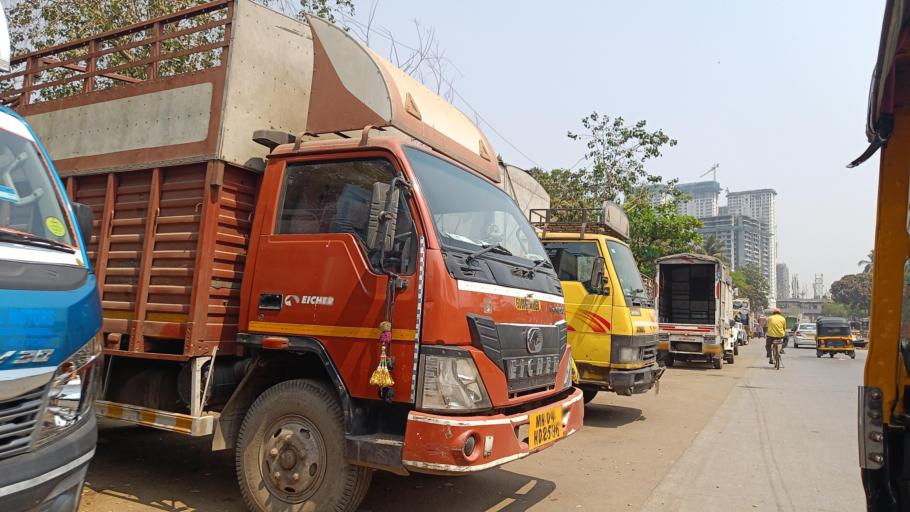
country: IN
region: Maharashtra
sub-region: Mumbai Suburban
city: Powai
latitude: 19.1494
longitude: 72.8408
